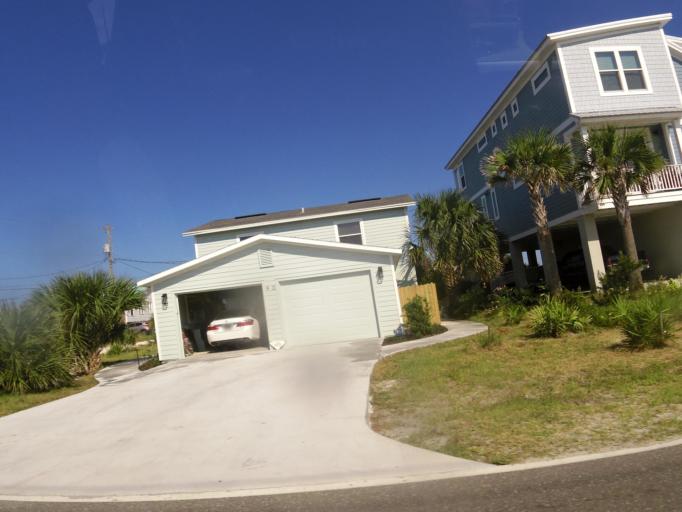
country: US
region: Florida
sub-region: Nassau County
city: Fernandina Beach
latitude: 30.6797
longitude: -81.4300
